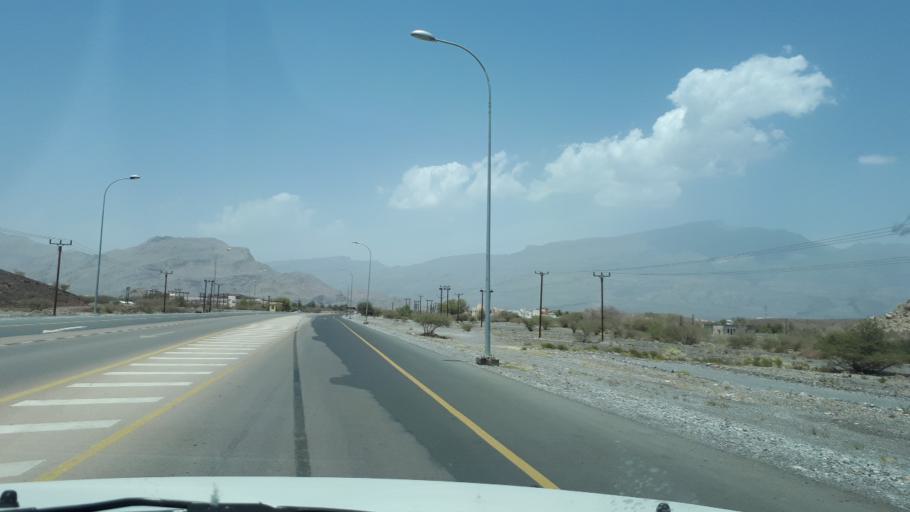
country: OM
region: Muhafazat ad Dakhiliyah
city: Bahla'
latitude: 23.0674
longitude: 57.2755
